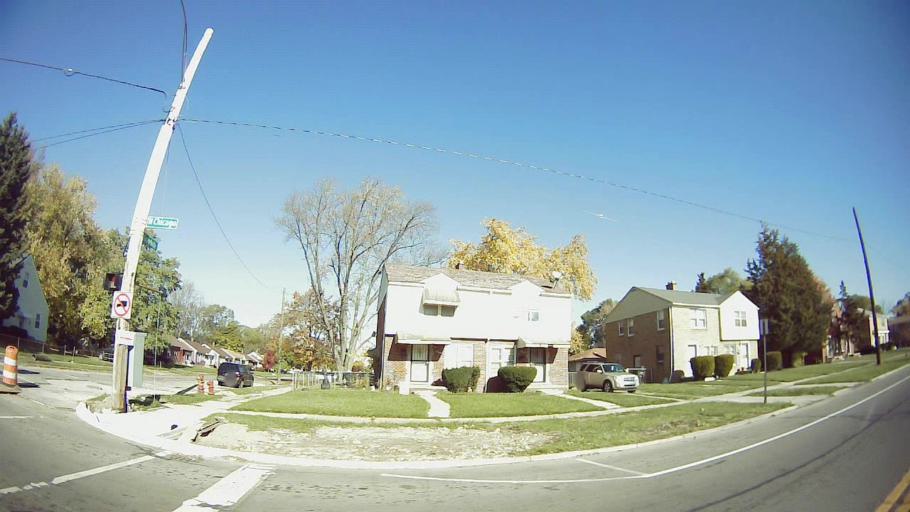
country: US
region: Michigan
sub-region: Wayne County
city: Dearborn Heights
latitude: 42.3648
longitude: -83.2305
